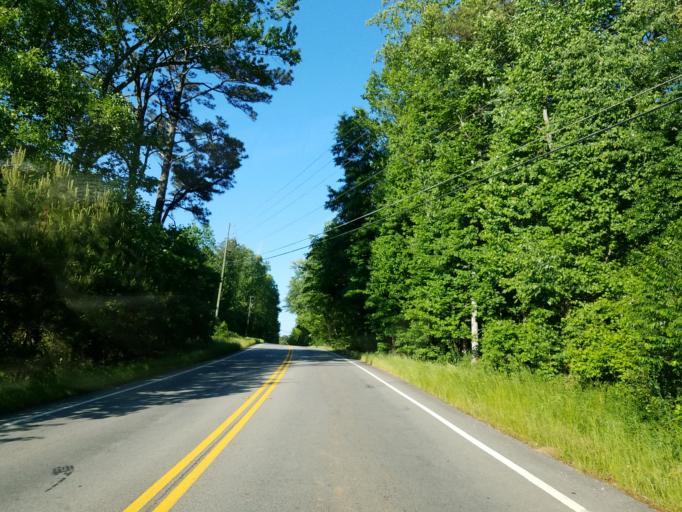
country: US
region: Georgia
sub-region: Carroll County
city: Villa Rica
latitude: 33.7291
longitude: -84.8751
